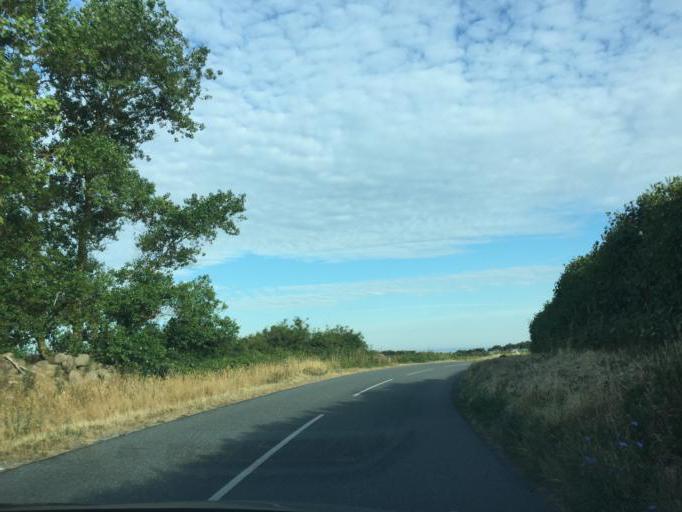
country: DK
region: South Denmark
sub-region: Assens Kommune
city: Harby
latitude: 55.1594
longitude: 9.9946
